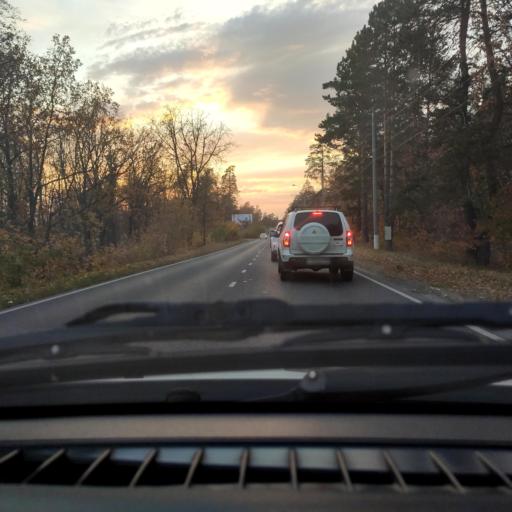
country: RU
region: Samara
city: Tol'yatti
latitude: 53.4733
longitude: 49.3942
